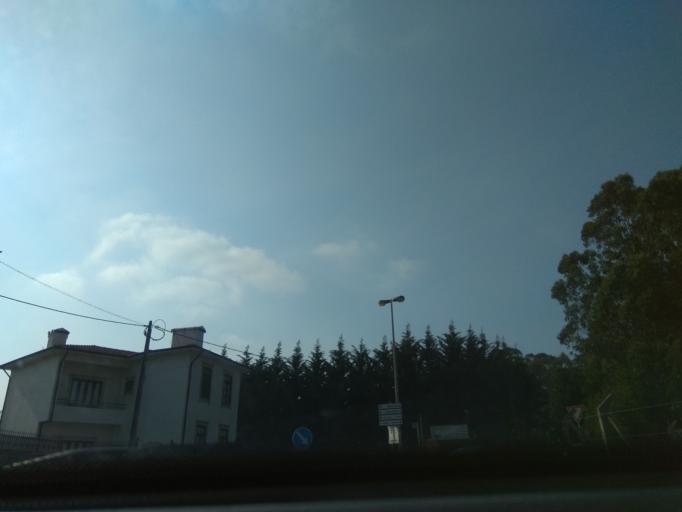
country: PT
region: Porto
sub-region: Maia
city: Anta
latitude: 41.2650
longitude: -8.6237
